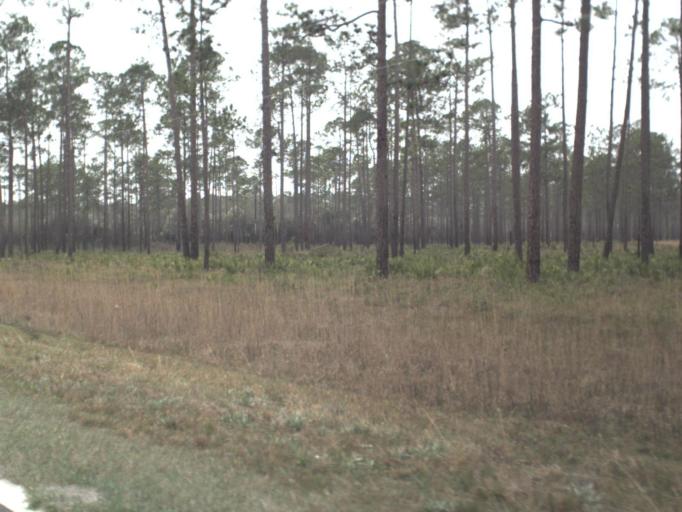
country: US
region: Florida
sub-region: Liberty County
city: Bristol
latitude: 30.2640
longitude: -84.8519
